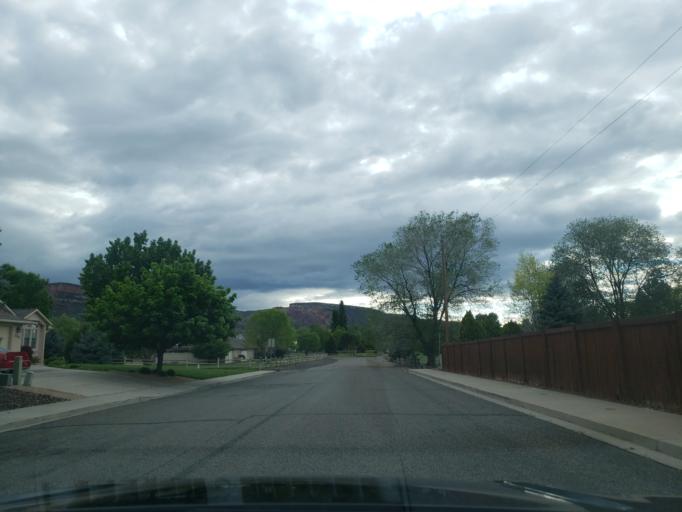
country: US
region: Colorado
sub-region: Mesa County
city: Redlands
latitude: 39.1033
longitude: -108.6727
